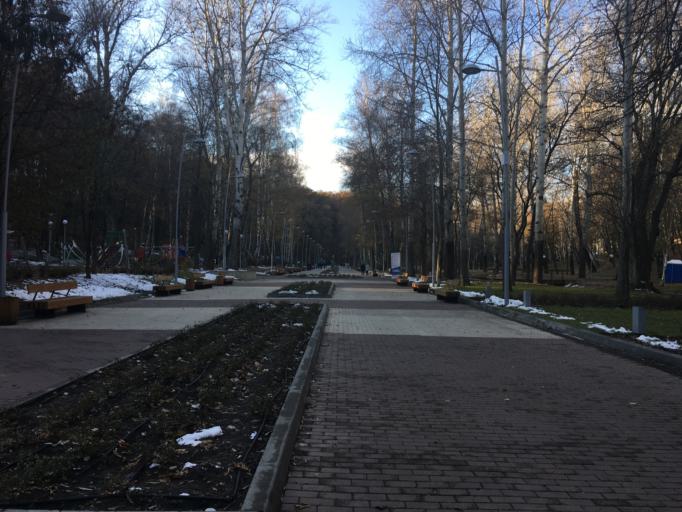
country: RU
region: Voronezj
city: Voronezh
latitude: 51.6967
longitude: 39.2216
